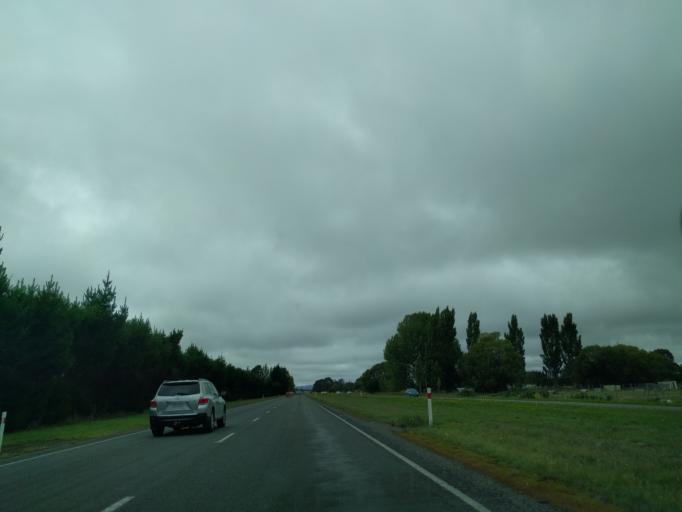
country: NZ
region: Canterbury
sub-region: Waimakariri District
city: Kaiapoi
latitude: -43.3966
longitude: 172.6414
